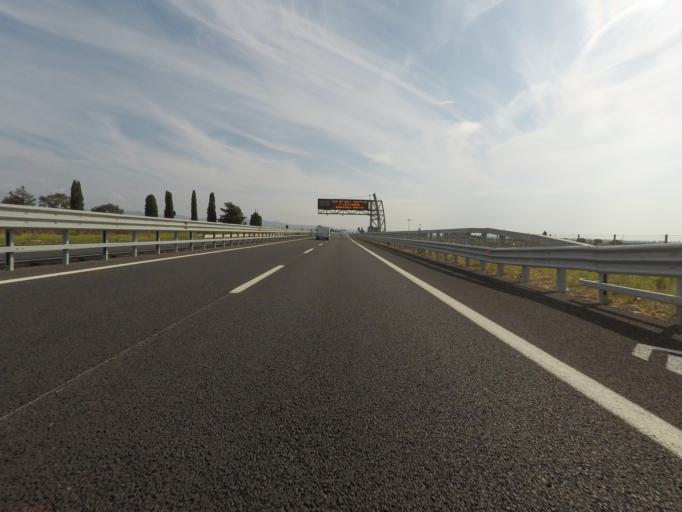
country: IT
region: Latium
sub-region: Provincia di Viterbo
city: Tarquinia
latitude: 42.2300
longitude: 11.7665
